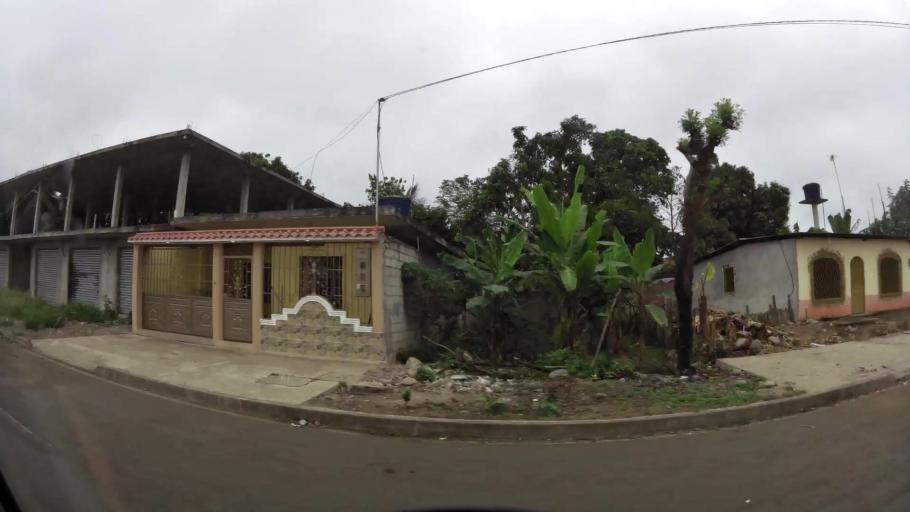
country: EC
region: El Oro
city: Pasaje
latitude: -3.3258
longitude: -79.8230
